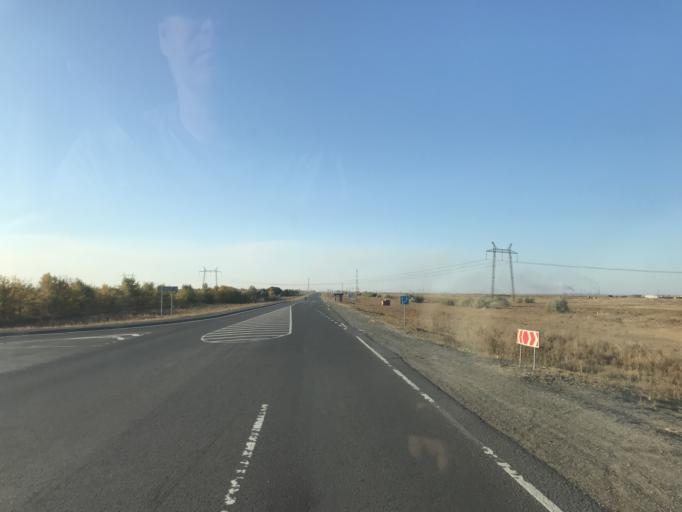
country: KZ
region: Pavlodar
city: Pavlodar
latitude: 52.0880
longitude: 77.1262
